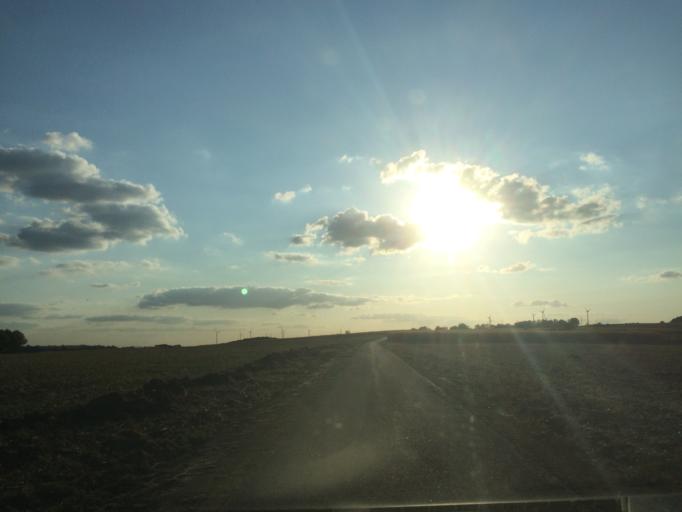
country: DE
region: Hesse
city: Trendelburg
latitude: 51.6122
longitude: 9.3943
